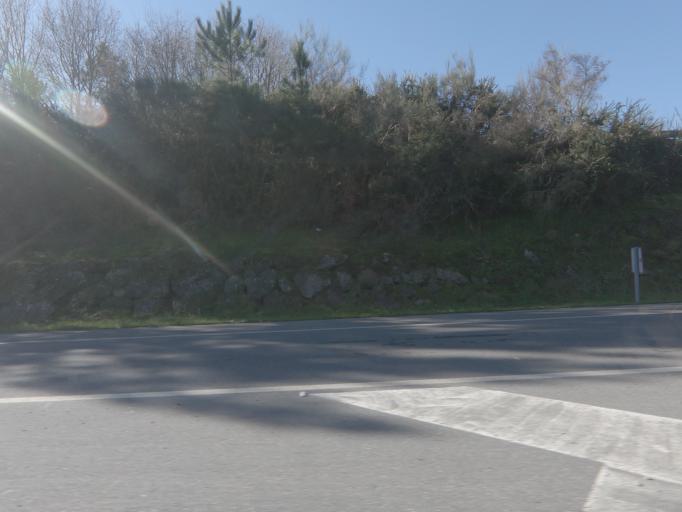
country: ES
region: Galicia
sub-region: Provincia de Pontevedra
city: Silleda
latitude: 42.6906
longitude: -8.2223
